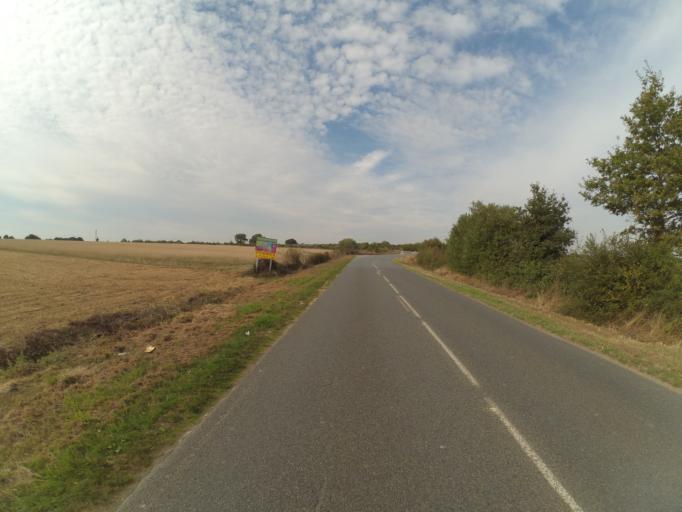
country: FR
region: Pays de la Loire
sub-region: Departement de Maine-et-Loire
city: Chemille-Melay
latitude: 47.2119
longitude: -0.7582
